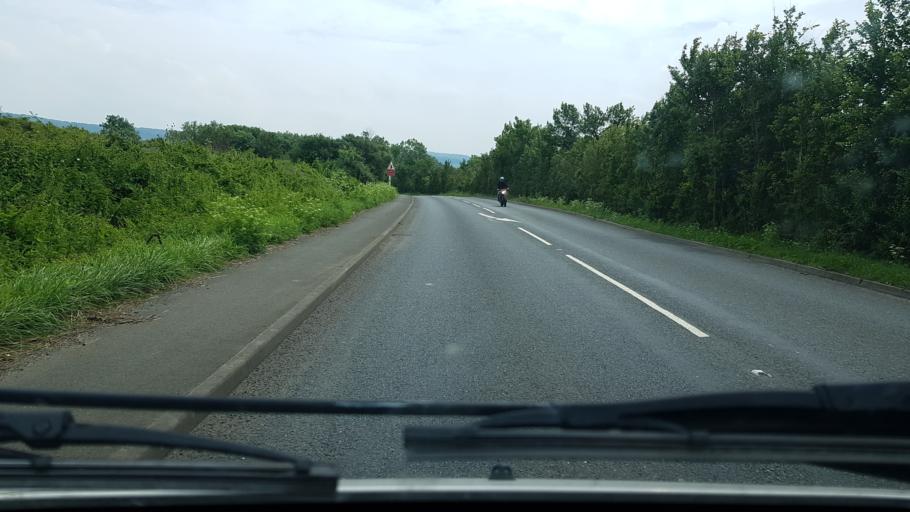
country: GB
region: England
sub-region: Worcestershire
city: Badsey
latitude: 52.0554
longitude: -1.8849
